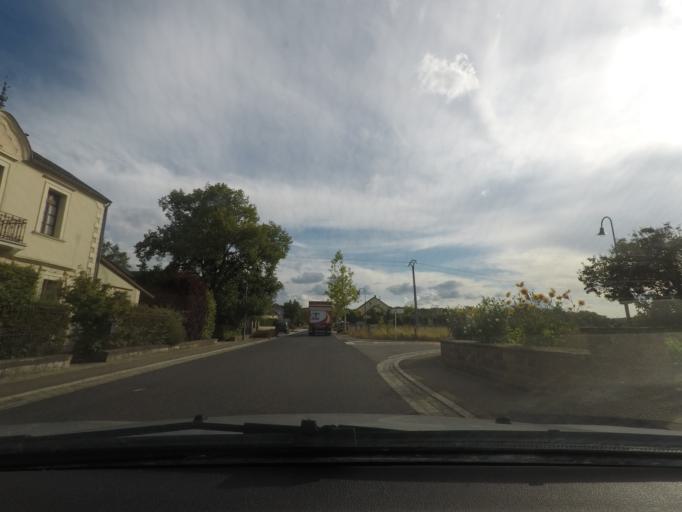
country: LU
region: Grevenmacher
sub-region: Canton d'Echternach
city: Consdorf
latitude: 49.7764
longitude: 6.3435
